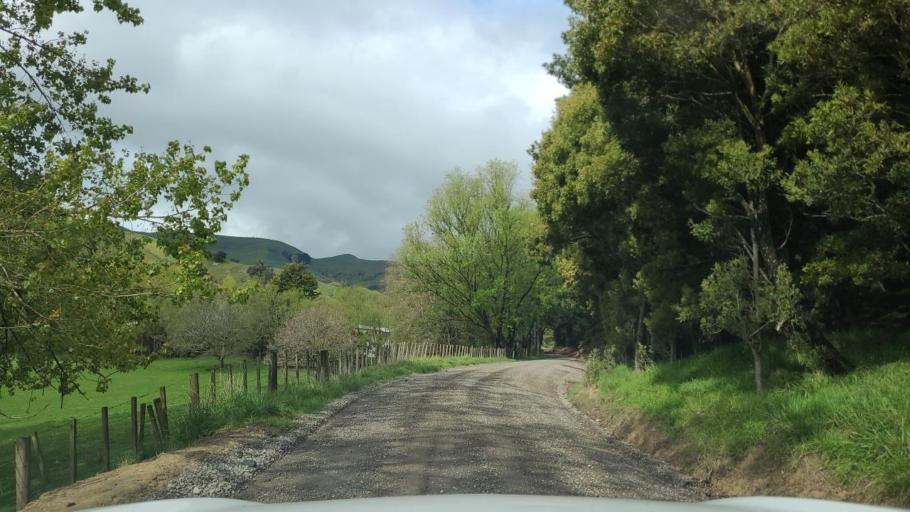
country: NZ
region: Wellington
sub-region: Masterton District
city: Masterton
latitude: -41.1697
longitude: 175.6219
